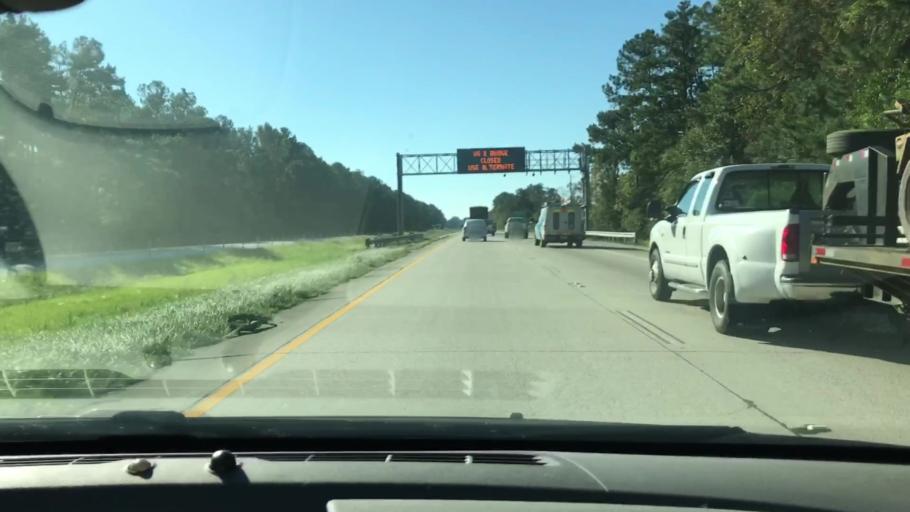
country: US
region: Louisiana
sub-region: Saint Tammany Parish
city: Pearl River
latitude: 30.3337
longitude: -89.7379
